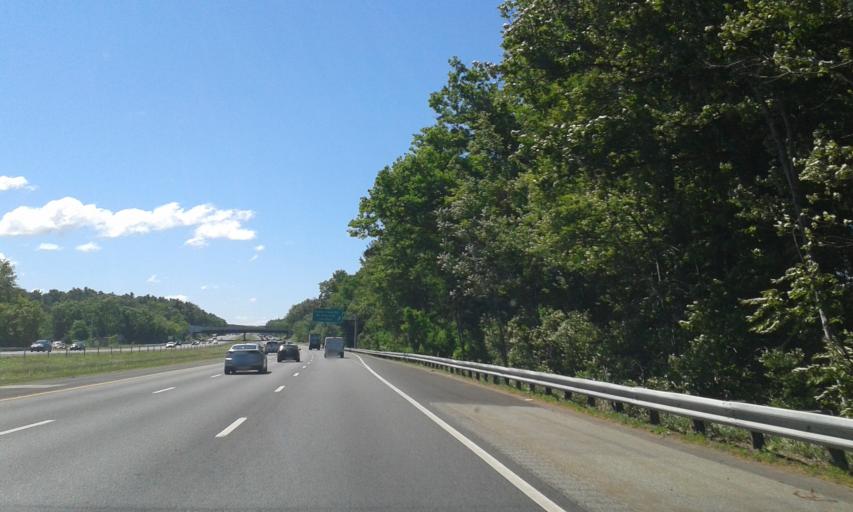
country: US
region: Massachusetts
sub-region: Middlesex County
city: Billerica
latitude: 42.5656
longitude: -71.3015
